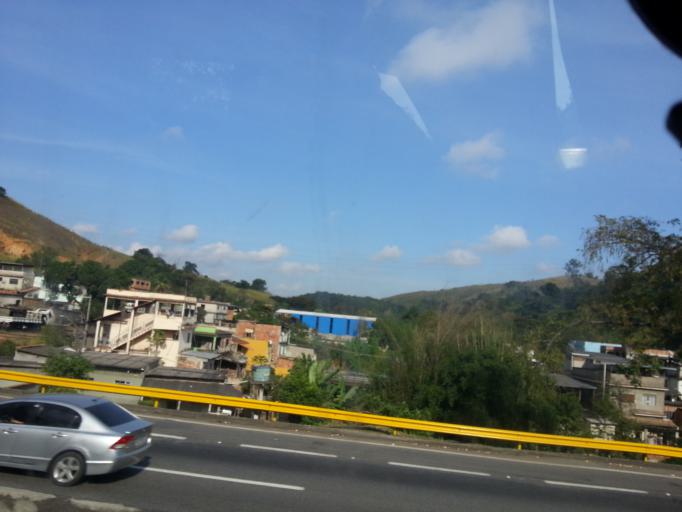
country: BR
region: Rio de Janeiro
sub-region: Barra Mansa
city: Barra Mansa
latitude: -22.5369
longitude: -44.1949
